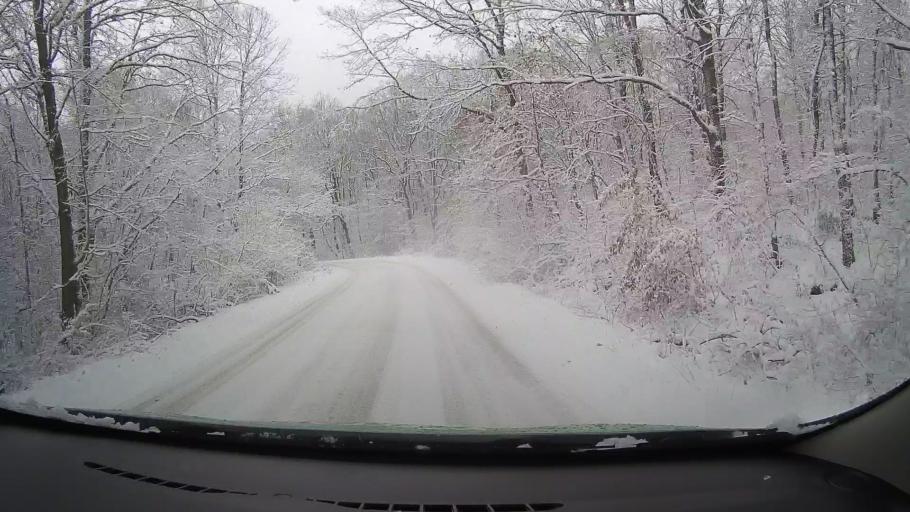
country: RO
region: Hunedoara
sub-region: Municipiul Deva
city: Deva
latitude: 45.8554
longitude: 22.8793
